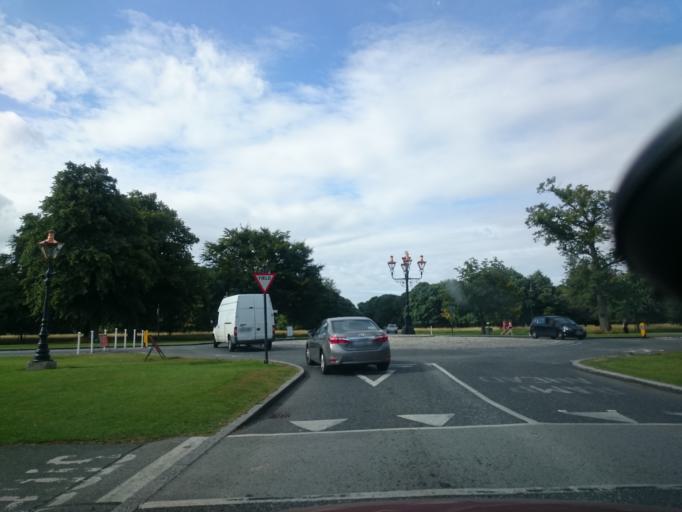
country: IE
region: Leinster
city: Chapelizod
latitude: 53.3668
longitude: -6.3411
